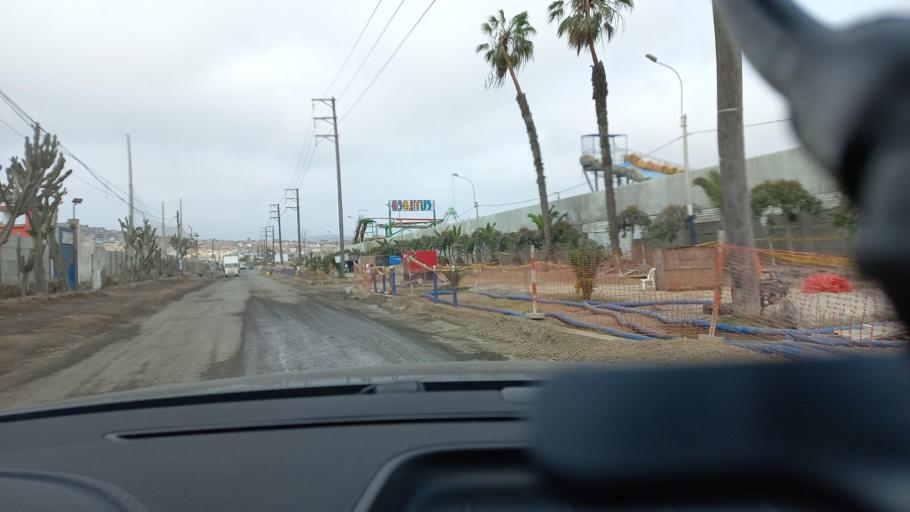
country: PE
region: Lima
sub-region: Lima
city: Surco
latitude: -12.2059
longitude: -77.0024
